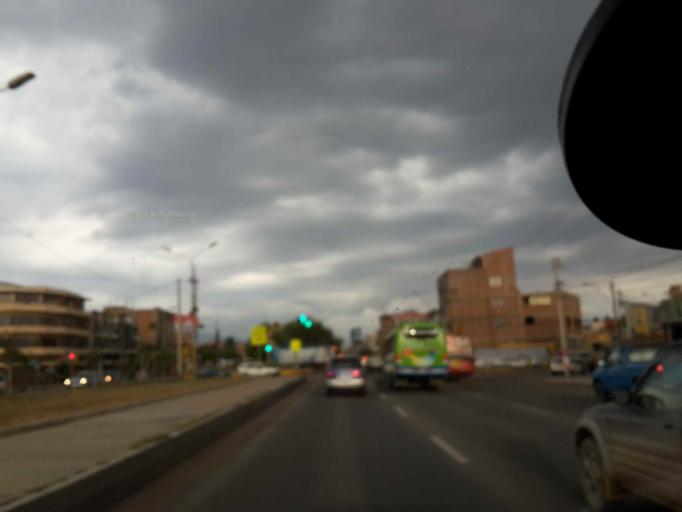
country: BO
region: Cochabamba
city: Sipe Sipe
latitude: -17.3944
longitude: -66.2873
